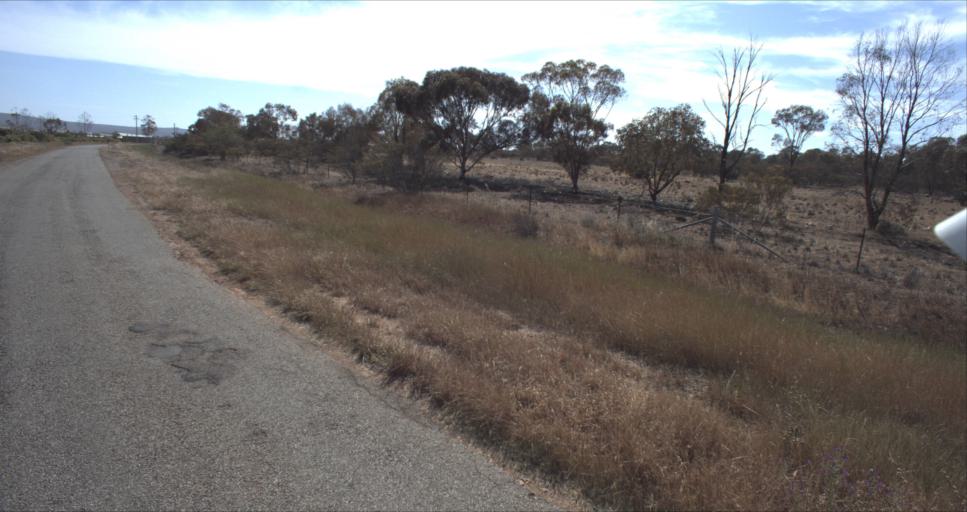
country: AU
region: New South Wales
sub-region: Leeton
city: Leeton
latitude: -34.5802
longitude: 146.4774
